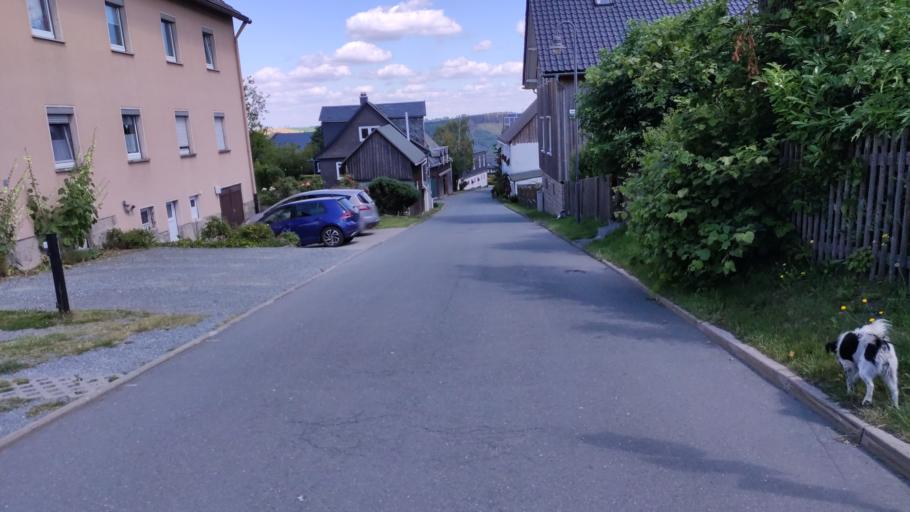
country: DE
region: Bavaria
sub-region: Upper Franconia
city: Ludwigsstadt
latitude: 50.5052
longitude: 11.4177
